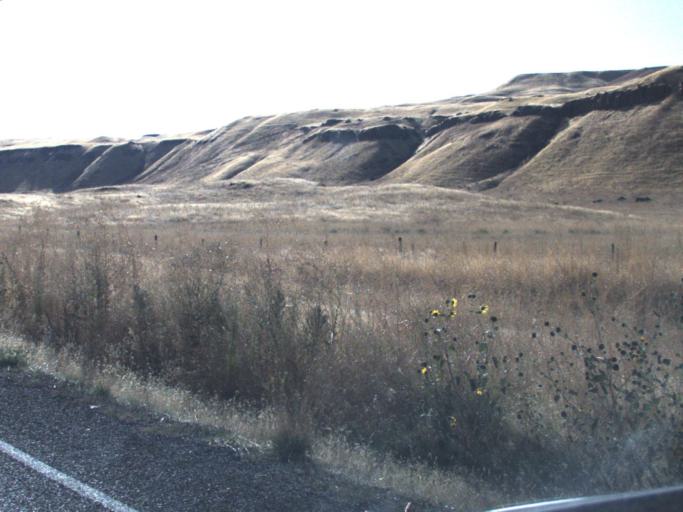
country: US
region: Washington
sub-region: Franklin County
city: Connell
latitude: 46.6467
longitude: -118.5831
